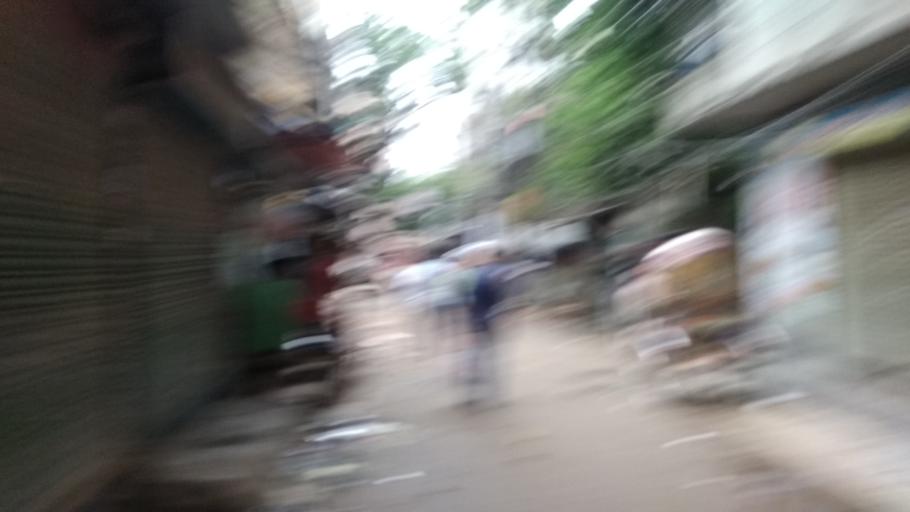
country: BD
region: Dhaka
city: Tungi
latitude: 23.8284
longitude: 90.3707
